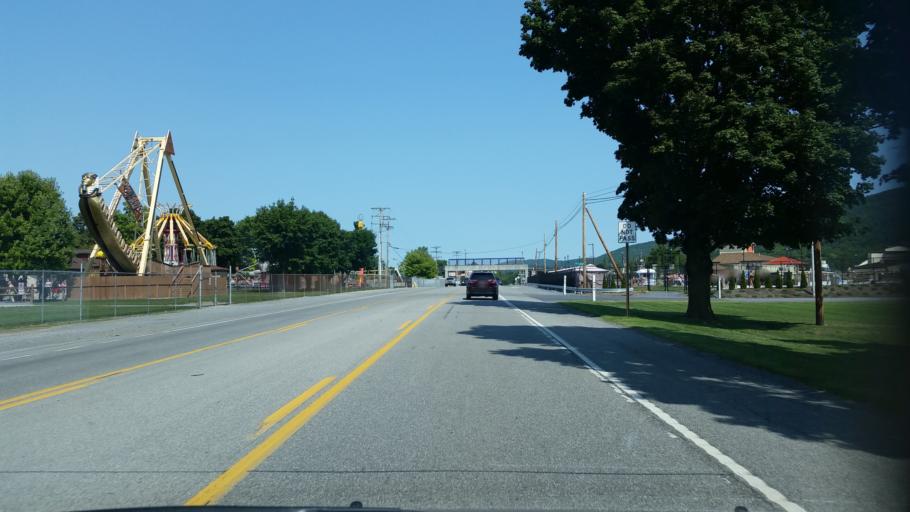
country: US
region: Pennsylvania
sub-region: Blair County
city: Tipton
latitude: 40.6295
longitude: -78.2927
